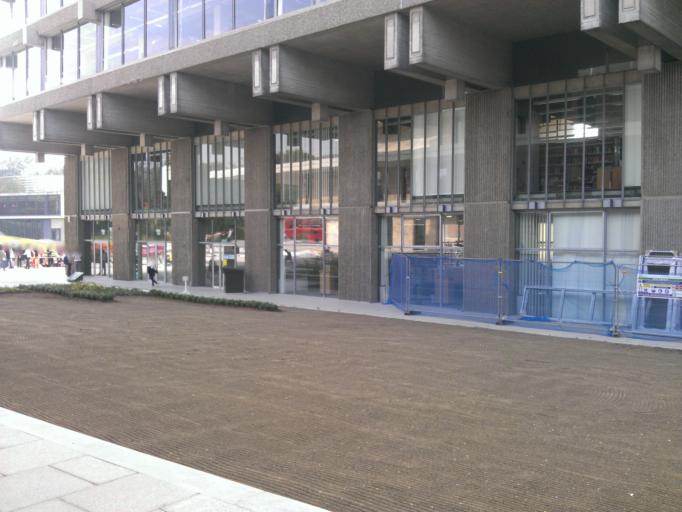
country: GB
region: England
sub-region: Essex
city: Rowhedge
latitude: 51.8774
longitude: 0.9469
